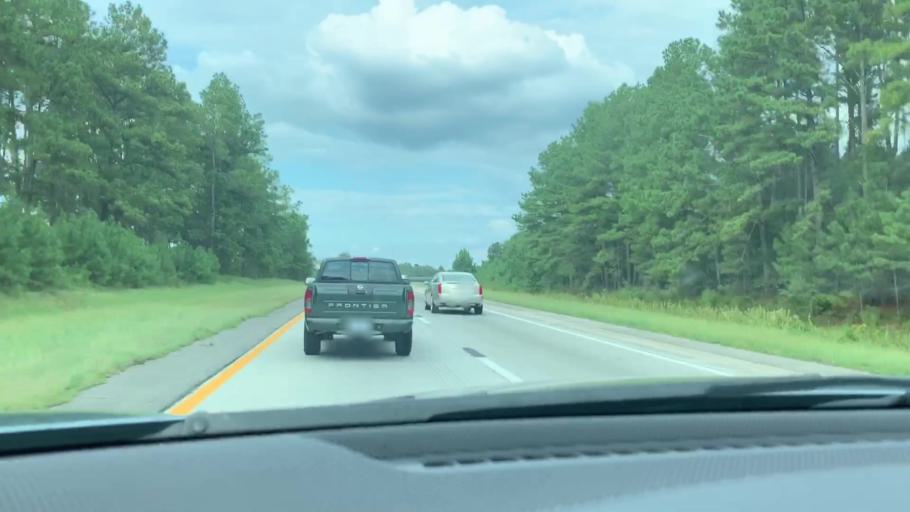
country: US
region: South Carolina
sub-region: Dorchester County
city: Saint George
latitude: 33.1245
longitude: -80.6401
